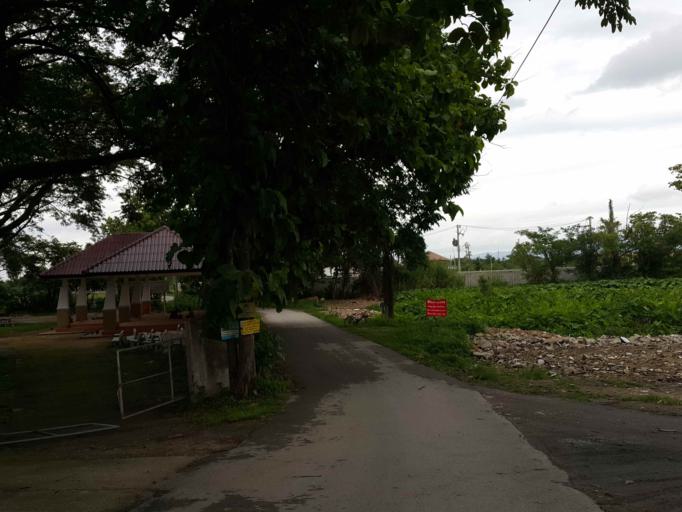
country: TH
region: Chiang Mai
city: San Sai
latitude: 18.8284
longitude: 99.0607
